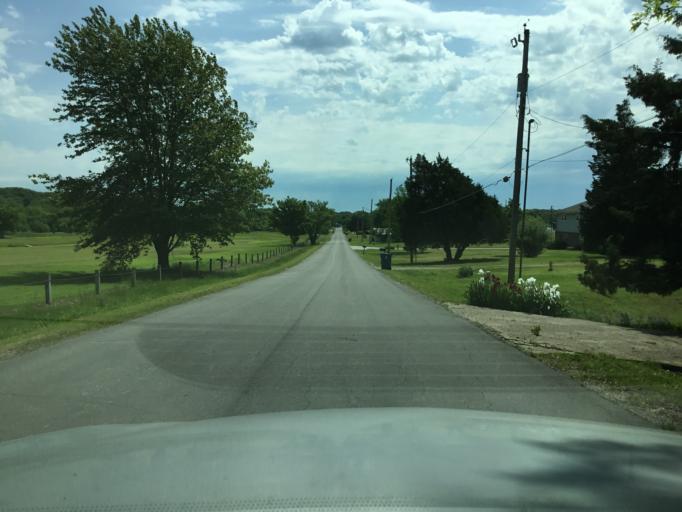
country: US
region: Kansas
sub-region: Montgomery County
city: Coffeyville
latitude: 37.0544
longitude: -95.6469
